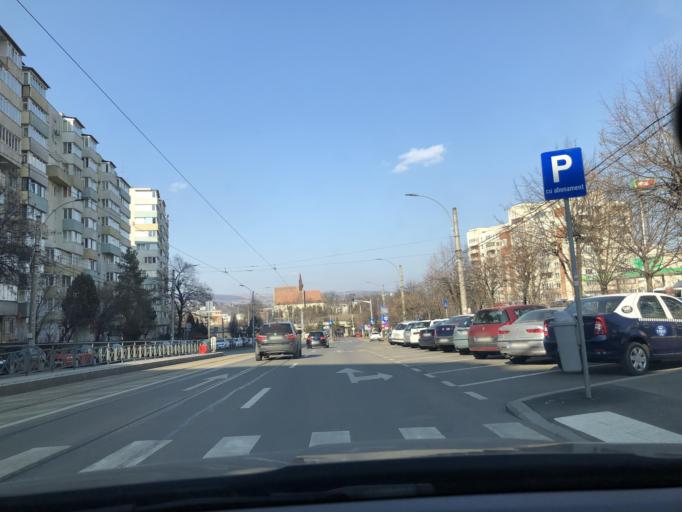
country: RO
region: Cluj
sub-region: Municipiul Cluj-Napoca
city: Cluj-Napoca
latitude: 46.7578
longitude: 23.5569
